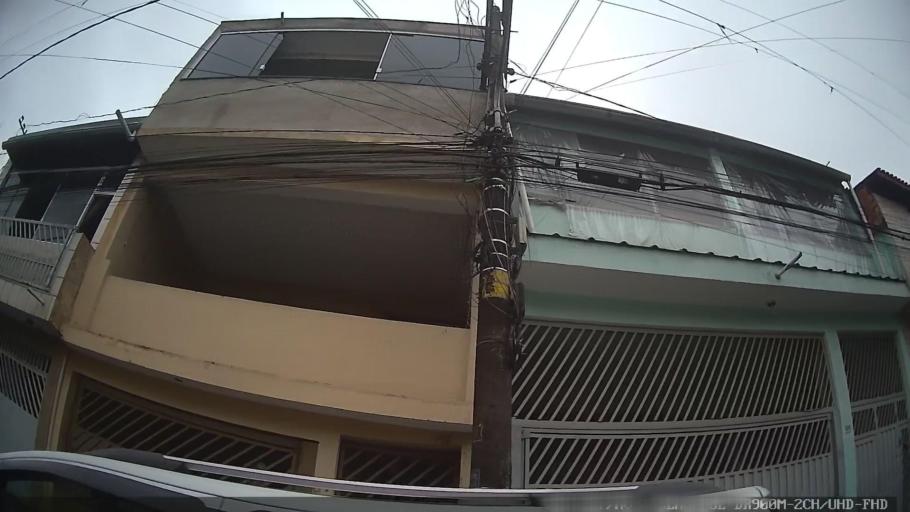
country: BR
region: Sao Paulo
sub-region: Caieiras
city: Caieiras
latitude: -23.4345
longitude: -46.7762
